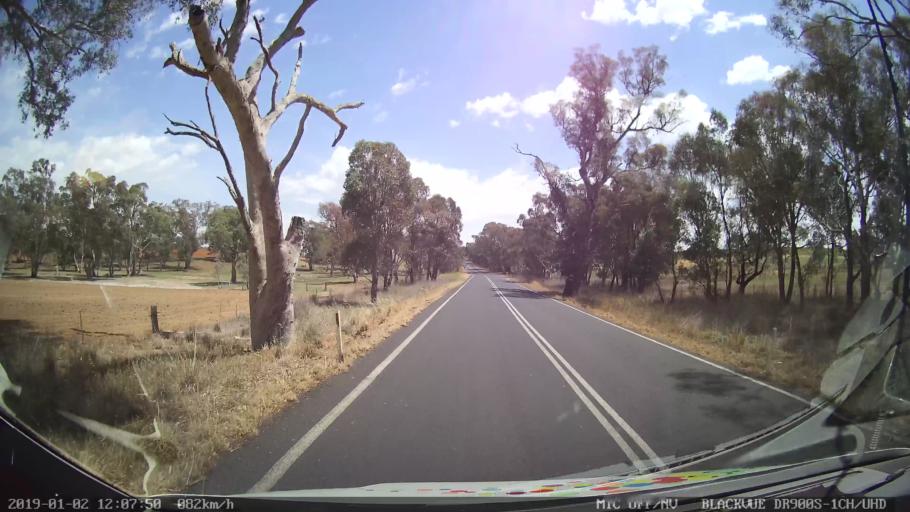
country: AU
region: New South Wales
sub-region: Young
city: Young
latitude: -34.4909
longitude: 148.2798
